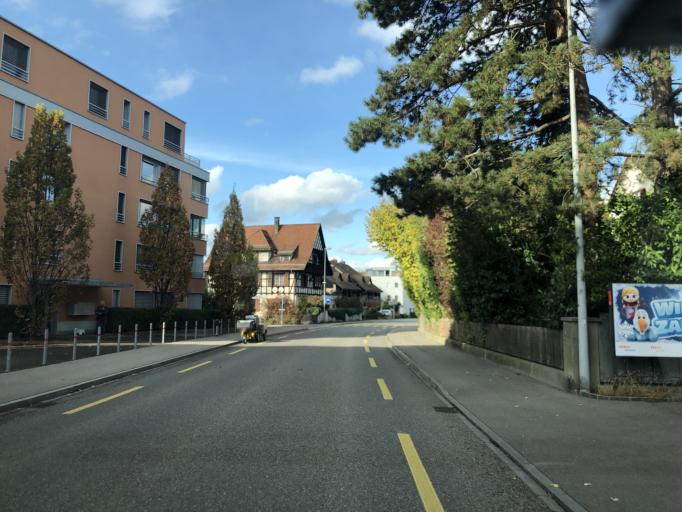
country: CH
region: Aargau
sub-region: Bezirk Baden
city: Wettingen
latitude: 47.4639
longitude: 8.3129
